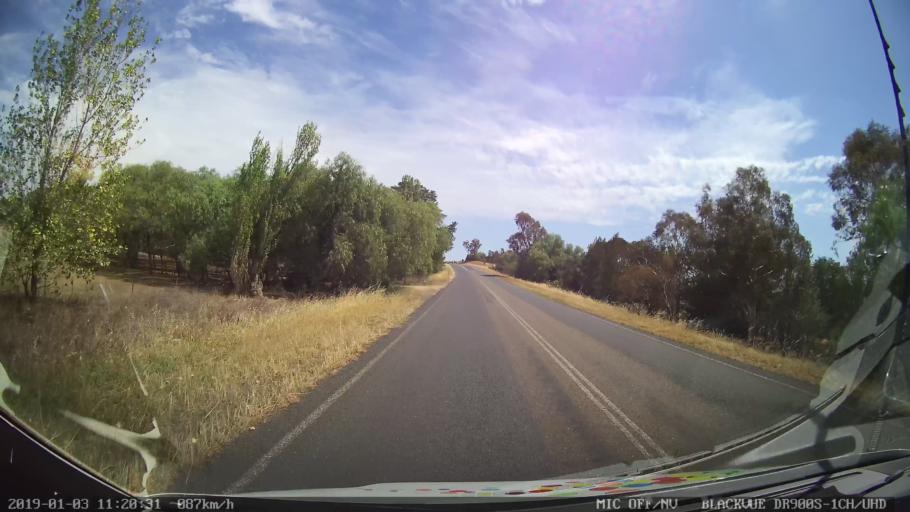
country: AU
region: New South Wales
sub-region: Young
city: Young
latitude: -34.1000
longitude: 148.2546
